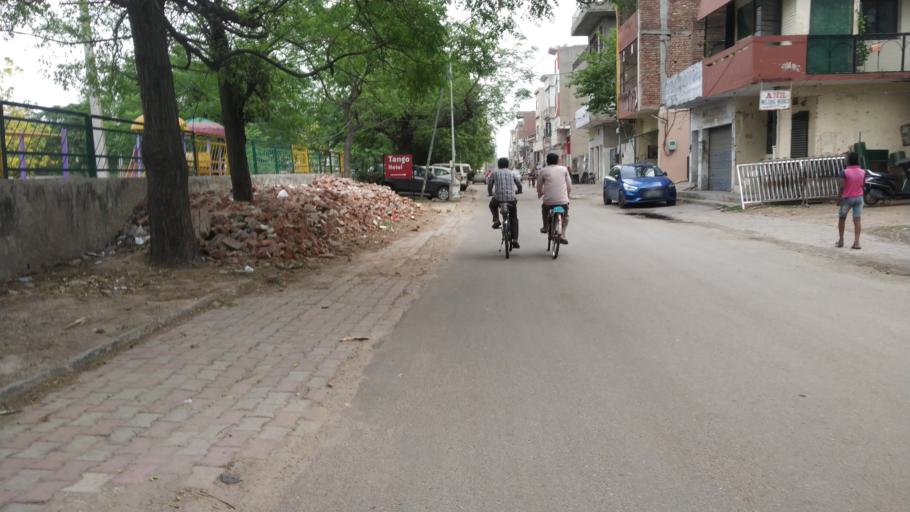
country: IN
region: Punjab
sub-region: Ajitgarh
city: Mohali
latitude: 30.7020
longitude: 76.7145
